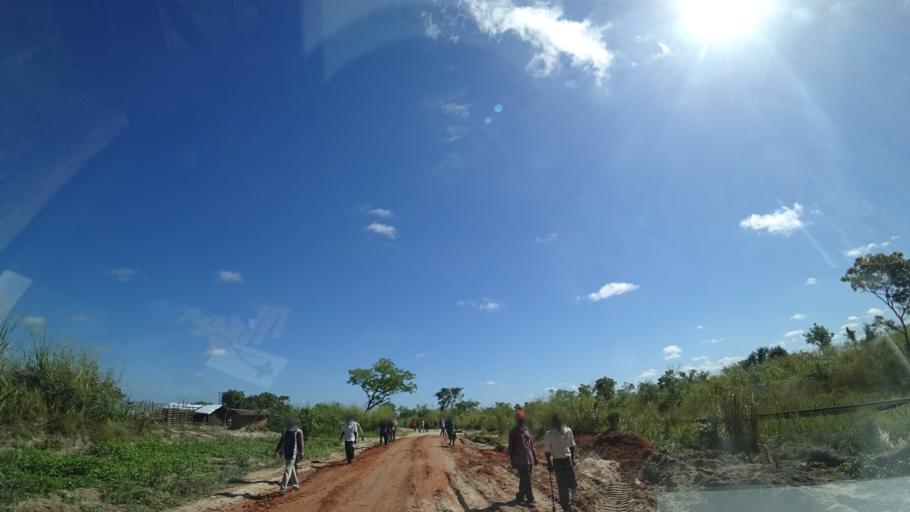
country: MZ
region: Sofala
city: Dondo
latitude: -19.2790
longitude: 34.6830
